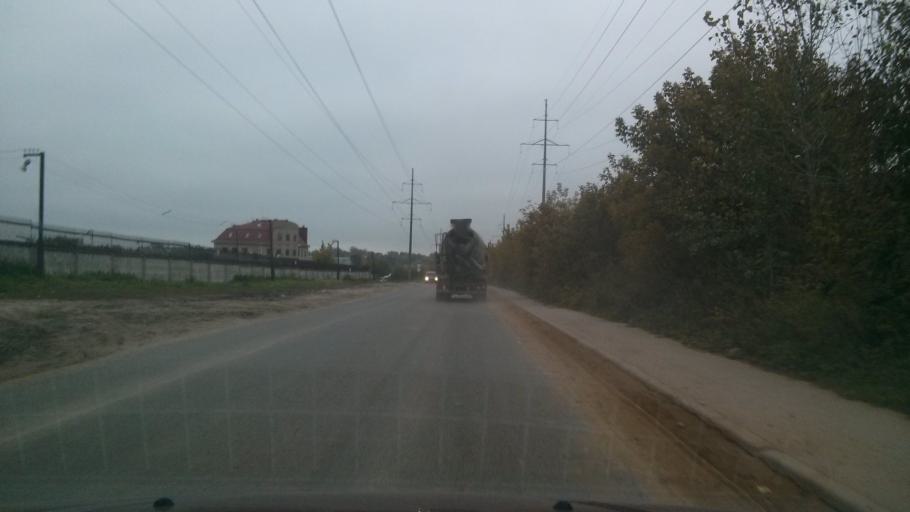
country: RU
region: Nizjnij Novgorod
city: Nizhniy Novgorod
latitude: 56.3037
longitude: 44.0092
